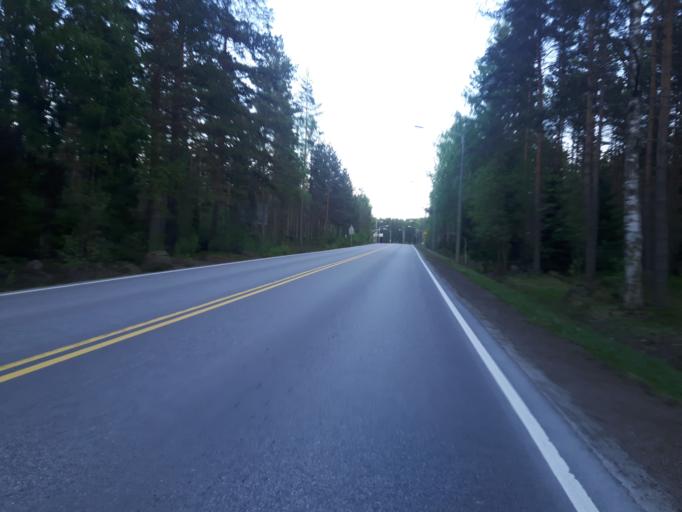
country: FI
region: Uusimaa
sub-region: Loviisa
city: Perna
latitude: 60.4545
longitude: 26.0934
